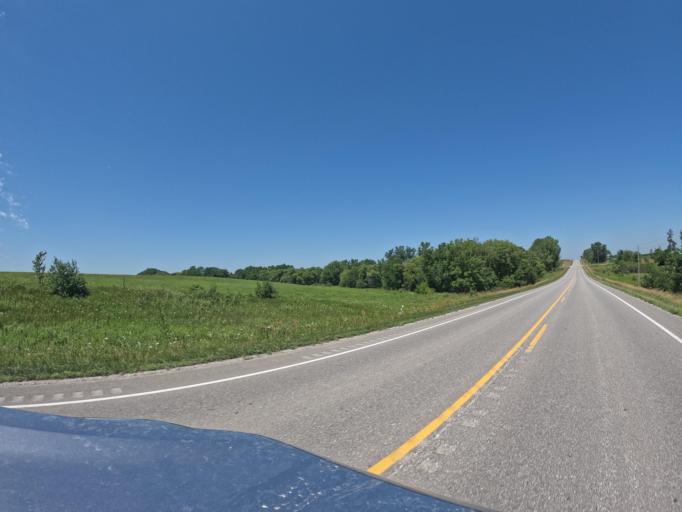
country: US
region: Iowa
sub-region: Keokuk County
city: Sigourney
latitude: 41.4640
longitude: -92.3552
